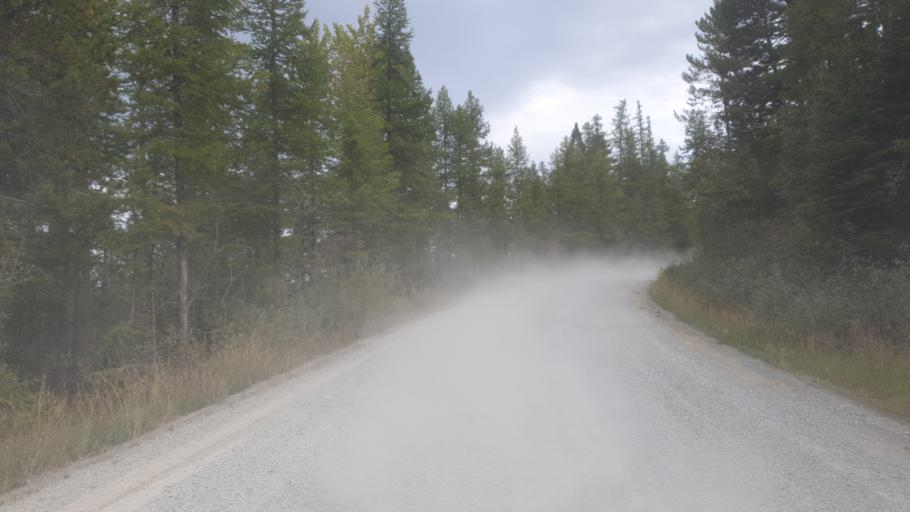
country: US
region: Montana
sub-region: Flathead County
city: Lakeside
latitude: 47.9920
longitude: -114.3285
